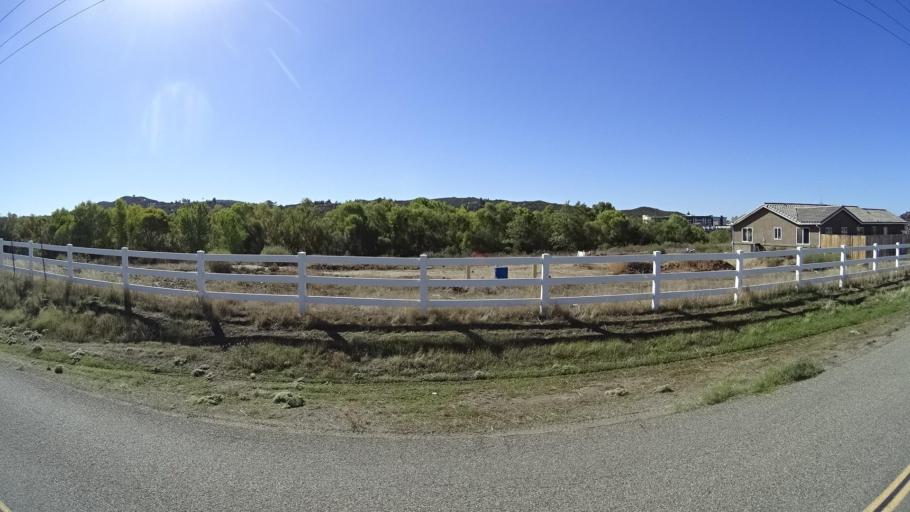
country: US
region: California
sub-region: San Diego County
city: Alpine
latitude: 32.8457
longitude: -116.7038
